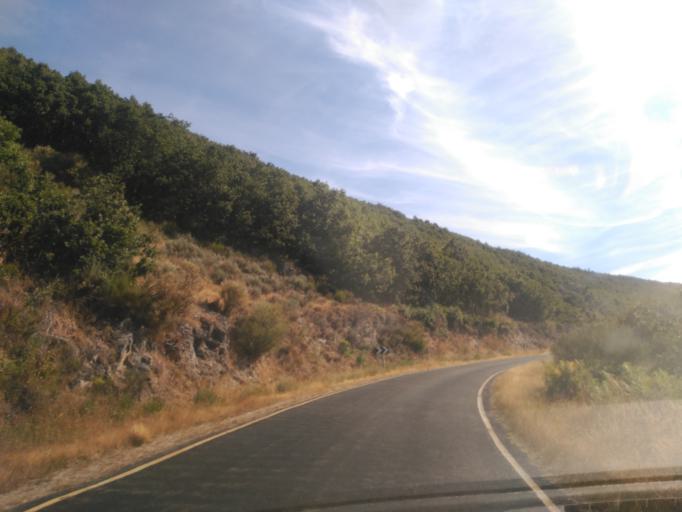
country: ES
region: Castille and Leon
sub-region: Provincia de Zamora
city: Galende
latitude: 42.1439
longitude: -6.7238
